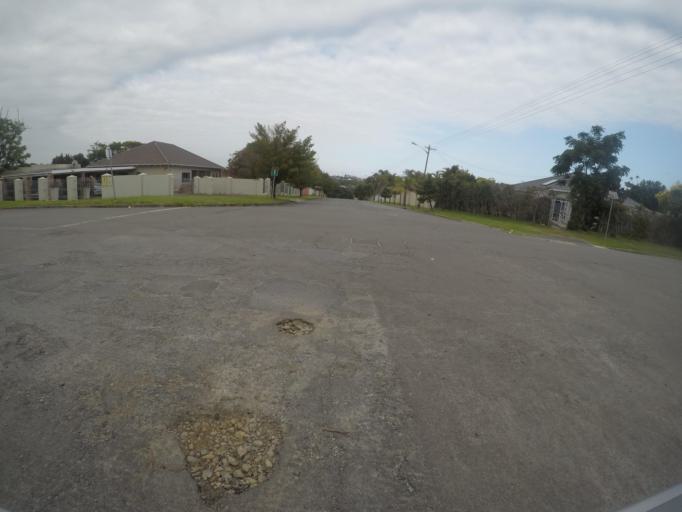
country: ZA
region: Eastern Cape
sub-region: Buffalo City Metropolitan Municipality
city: East London
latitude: -32.9907
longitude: 27.8975
